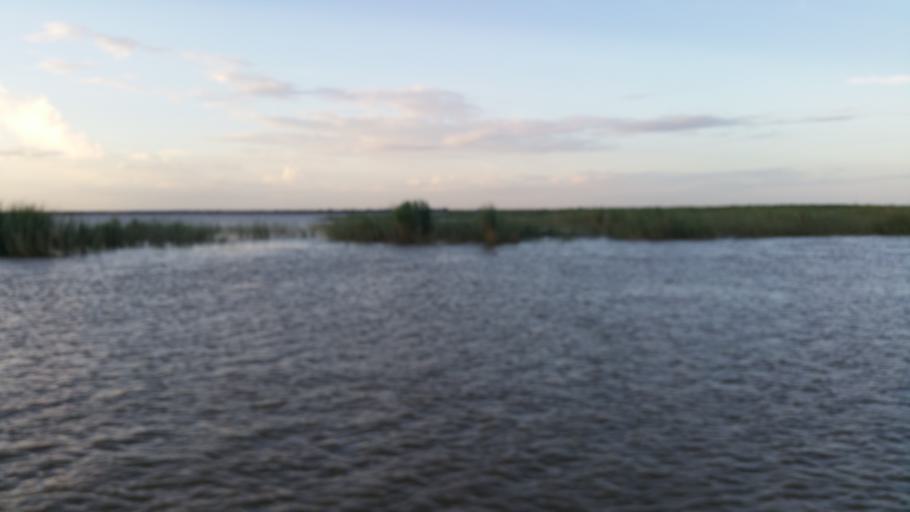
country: MM
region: Magway
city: Pakokku
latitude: 21.1949
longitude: 94.8756
